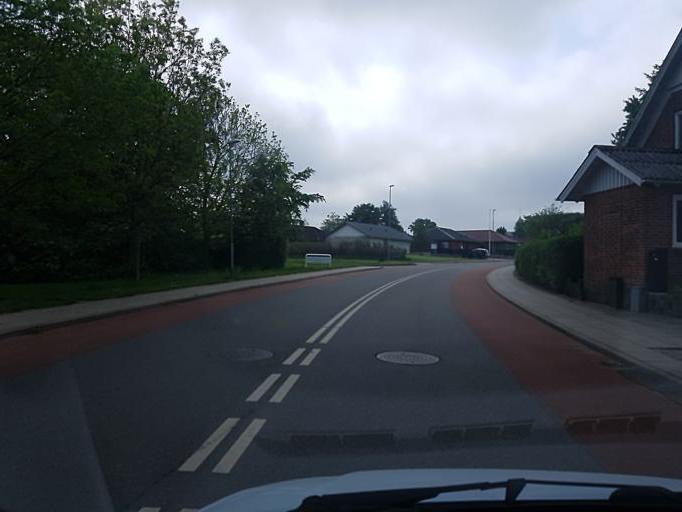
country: DK
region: South Denmark
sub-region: Esbjerg Kommune
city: Esbjerg
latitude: 55.5363
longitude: 8.4816
